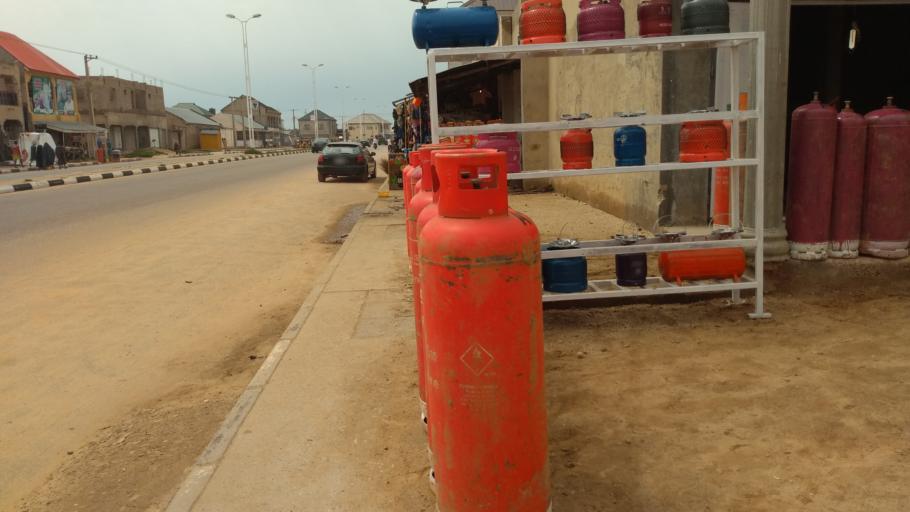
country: NG
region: Katsina
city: Katsina
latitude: 12.9757
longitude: 7.6419
